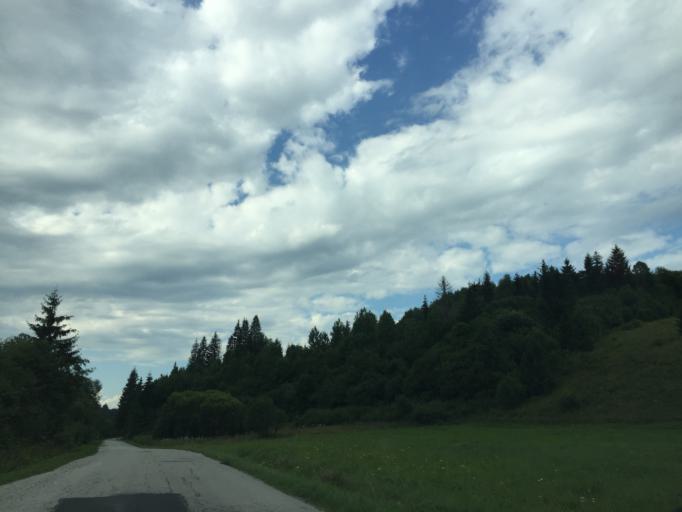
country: SK
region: Zilinsky
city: Namestovo
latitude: 49.3977
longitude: 19.3350
